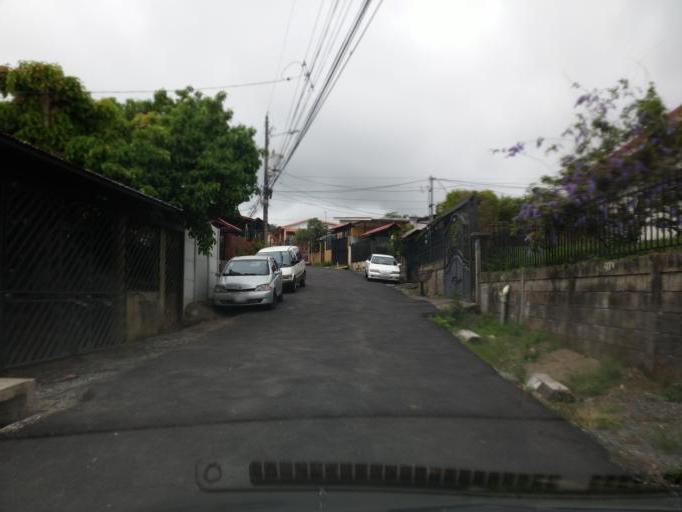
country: CR
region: Heredia
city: San Josecito
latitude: 10.0303
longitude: -84.1212
